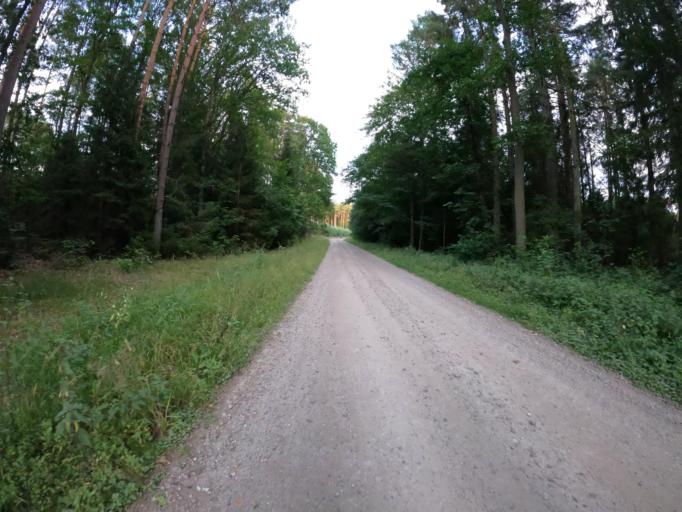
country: PL
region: West Pomeranian Voivodeship
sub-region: Powiat koszalinski
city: Sianow
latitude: 54.1060
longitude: 16.3683
